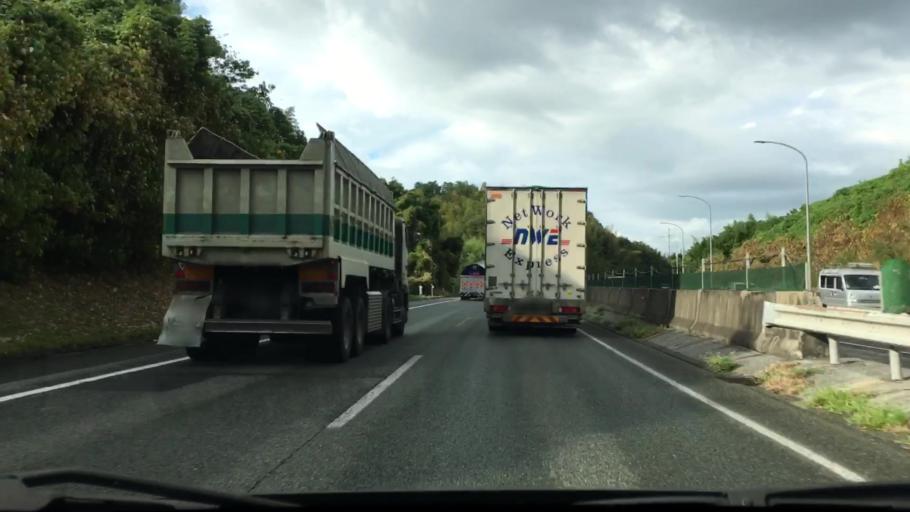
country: JP
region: Fukuoka
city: Nishifukuma
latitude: 33.7463
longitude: 130.5275
